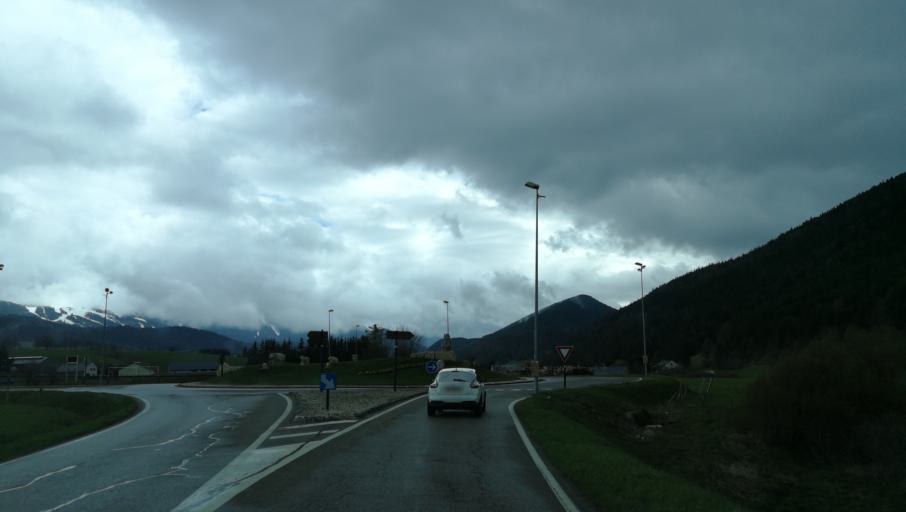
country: FR
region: Rhone-Alpes
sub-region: Departement de l'Isere
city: Villard-de-Lans
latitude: 45.0907
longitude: 5.5557
